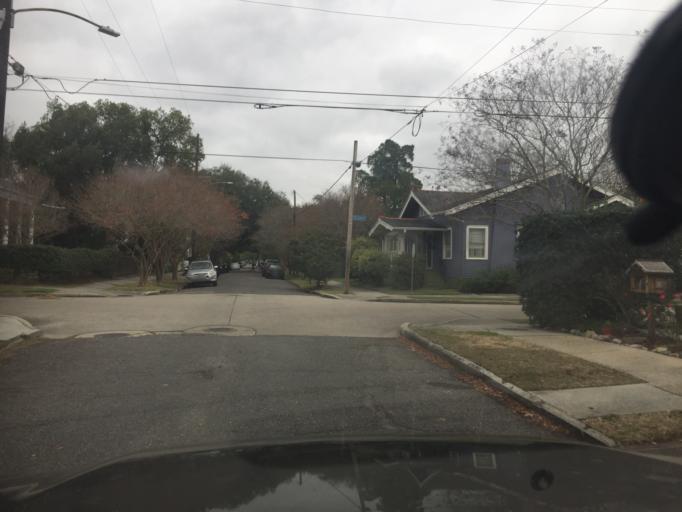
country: US
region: Louisiana
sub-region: Orleans Parish
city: New Orleans
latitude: 29.9786
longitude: -90.0841
